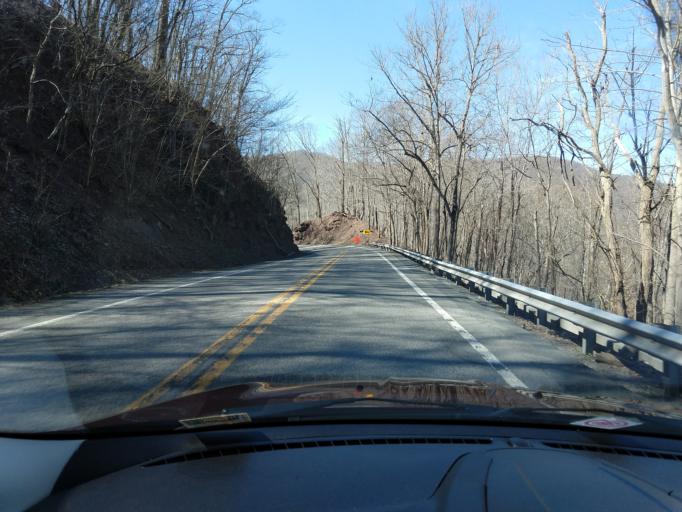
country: US
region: West Virginia
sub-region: Summers County
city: Hinton
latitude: 37.7498
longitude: -80.9083
